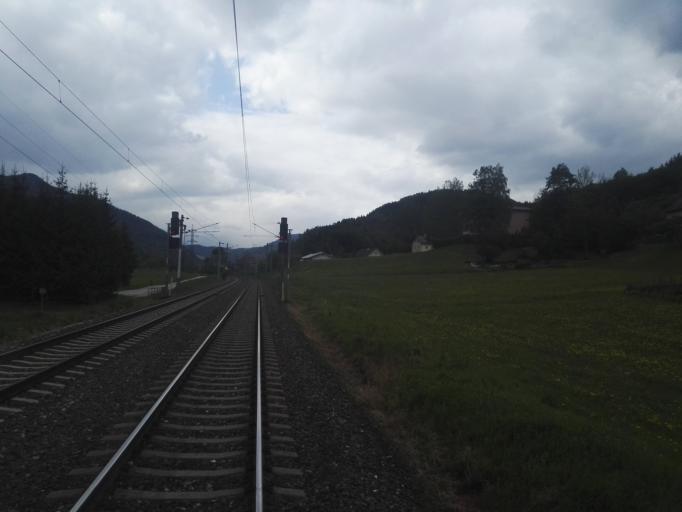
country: AT
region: Styria
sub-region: Politischer Bezirk Graz-Umgebung
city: Rothelstein
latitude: 47.3255
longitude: 15.3662
